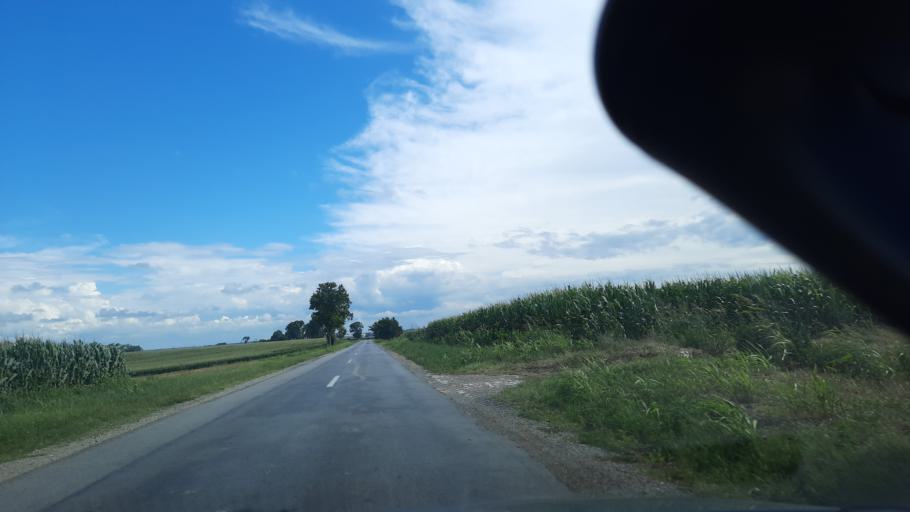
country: RS
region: Autonomna Pokrajina Vojvodina
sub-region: Sremski Okrug
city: Sremska Mitrovica
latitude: 45.0571
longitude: 19.5997
